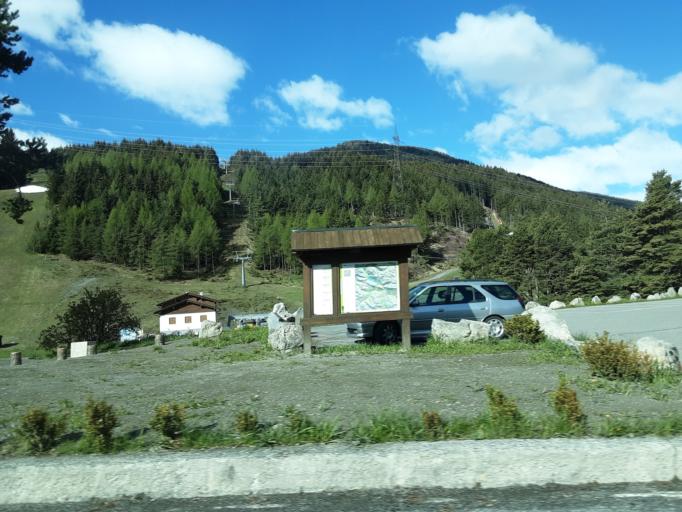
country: IT
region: Lombardy
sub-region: Provincia di Sondrio
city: Bormio
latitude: 46.4765
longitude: 10.3510
